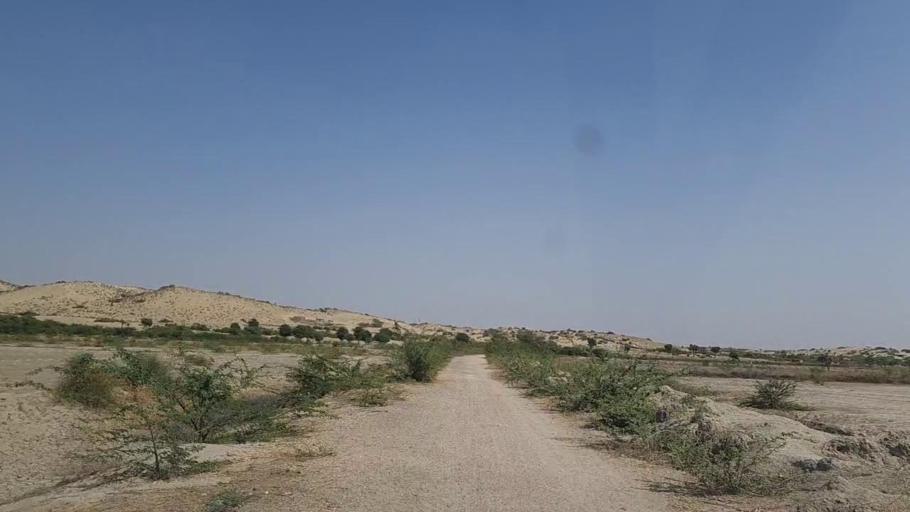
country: PK
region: Sindh
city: Naukot
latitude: 24.6299
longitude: 69.2927
